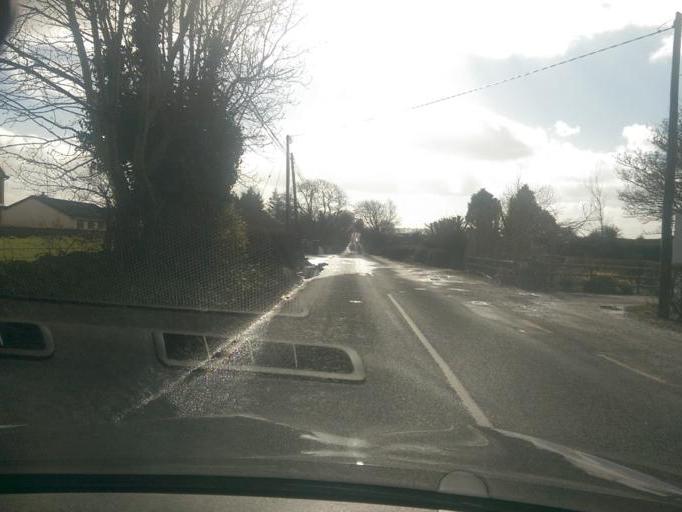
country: IE
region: Connaught
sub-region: County Galway
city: Athenry
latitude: 53.3652
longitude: -8.7009
